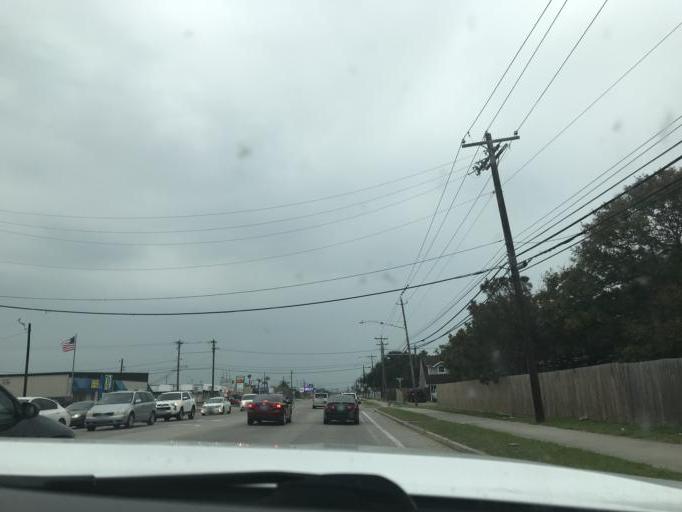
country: US
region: Texas
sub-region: Nueces County
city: Corpus Christi
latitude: 27.7004
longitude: -97.3744
